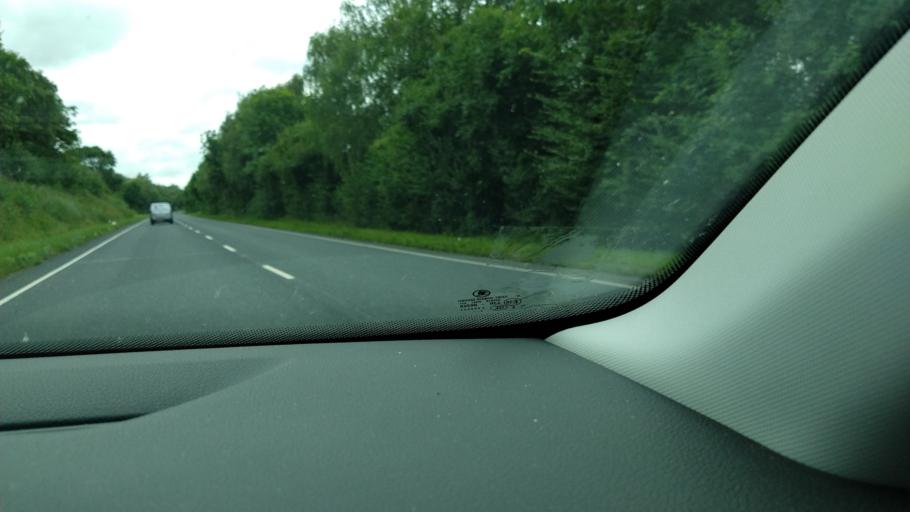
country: GB
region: England
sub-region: North Yorkshire
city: Camblesforth
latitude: 53.7232
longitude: -0.9832
